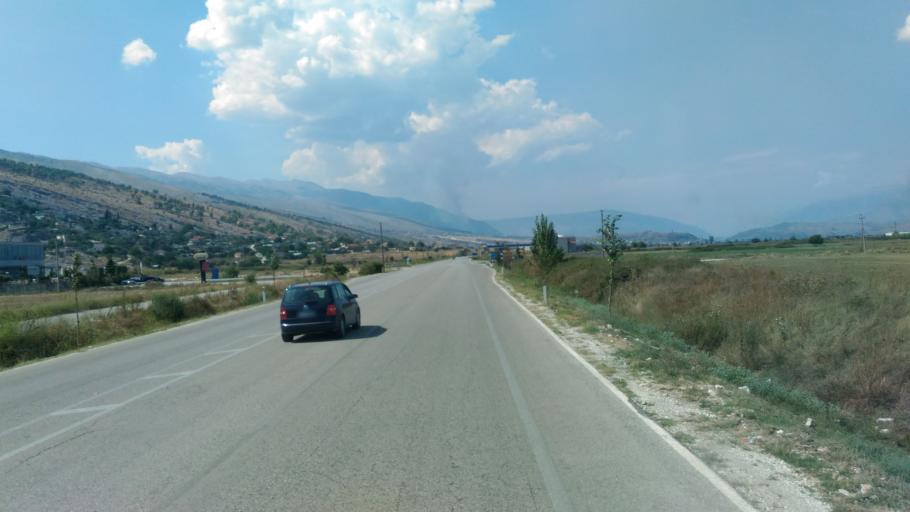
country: AL
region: Gjirokaster
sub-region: Rrethi i Gjirokastres
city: Dervician
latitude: 40.0123
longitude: 20.2015
